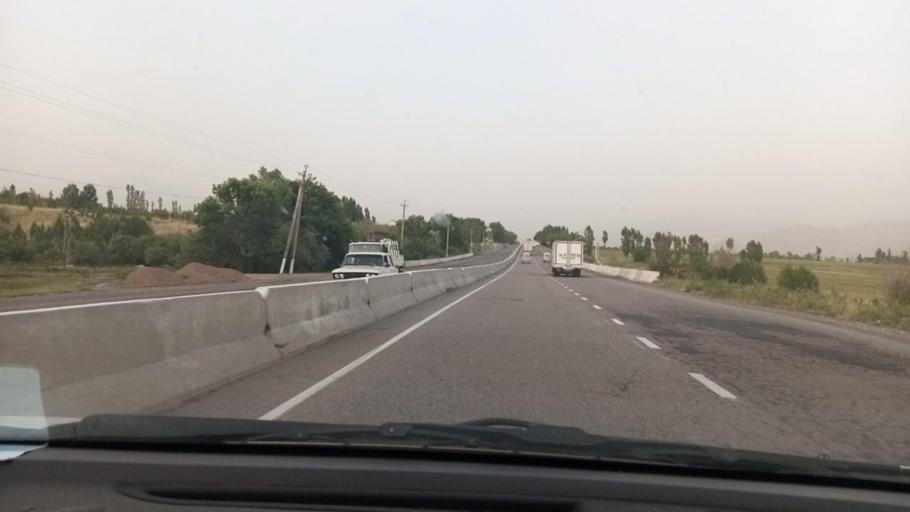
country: UZ
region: Toshkent
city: Angren
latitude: 40.9690
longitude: 69.9796
